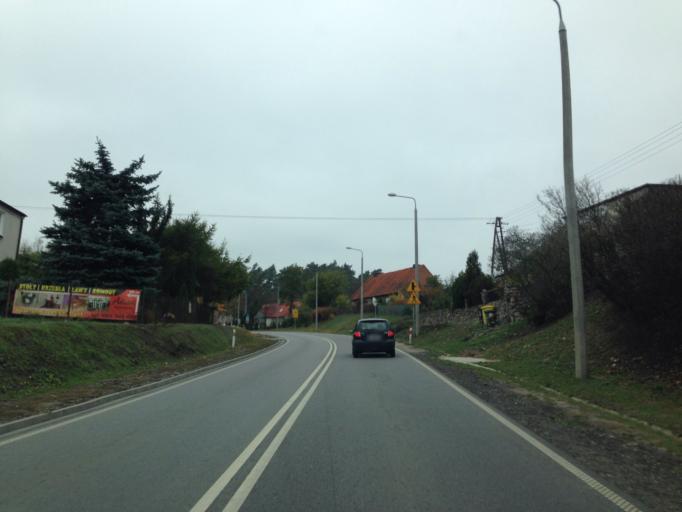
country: PL
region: Kujawsko-Pomorskie
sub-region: Powiat grudziadzki
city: Radzyn Chelminski
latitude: 53.4379
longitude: 18.8492
